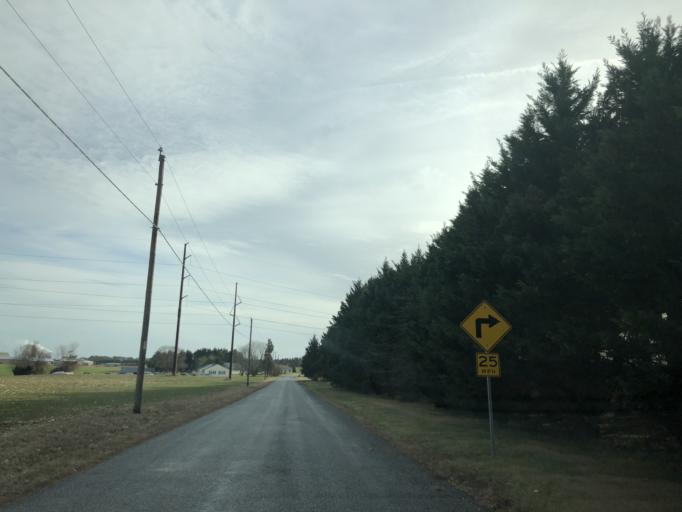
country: US
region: Delaware
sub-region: New Castle County
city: Middletown
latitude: 39.4530
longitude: -75.6366
